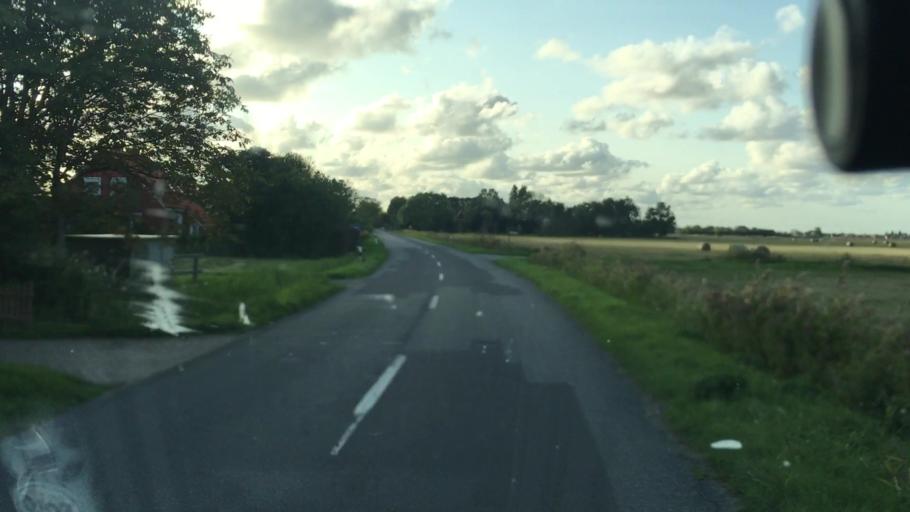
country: DE
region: Lower Saxony
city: Neuharlingersiel
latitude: 53.6803
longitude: 7.7113
